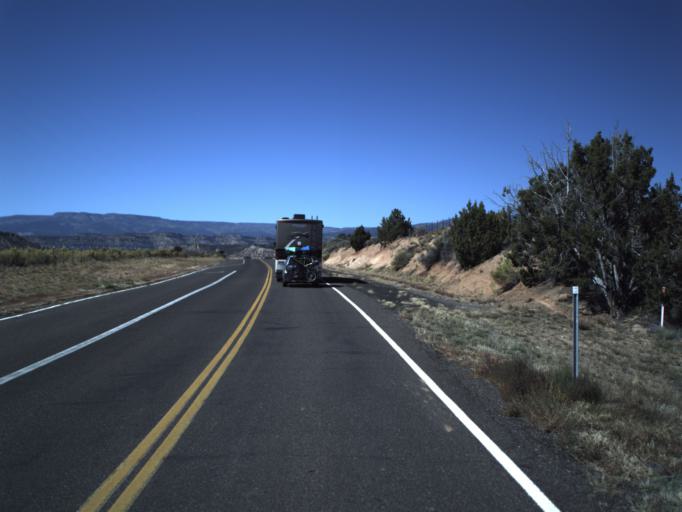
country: US
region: Utah
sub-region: Wayne County
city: Loa
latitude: 37.7575
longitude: -111.5722
